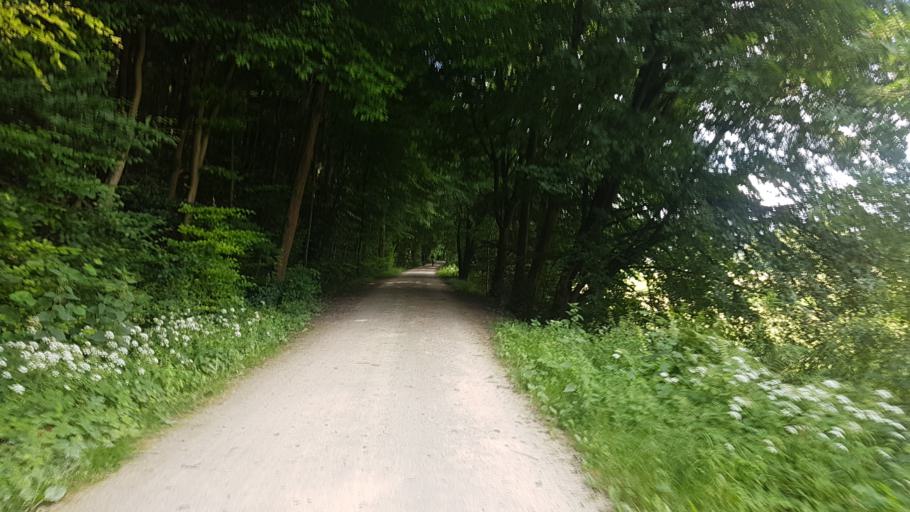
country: DE
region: Bavaria
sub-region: Upper Bavaria
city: Eichstaett
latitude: 48.8820
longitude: 11.2538
